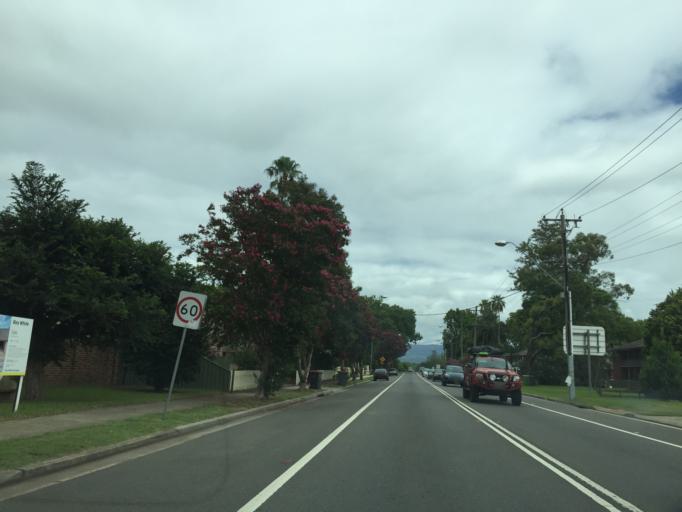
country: AU
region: New South Wales
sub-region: Hawkesbury
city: Richmond
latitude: -33.5965
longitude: 150.7462
